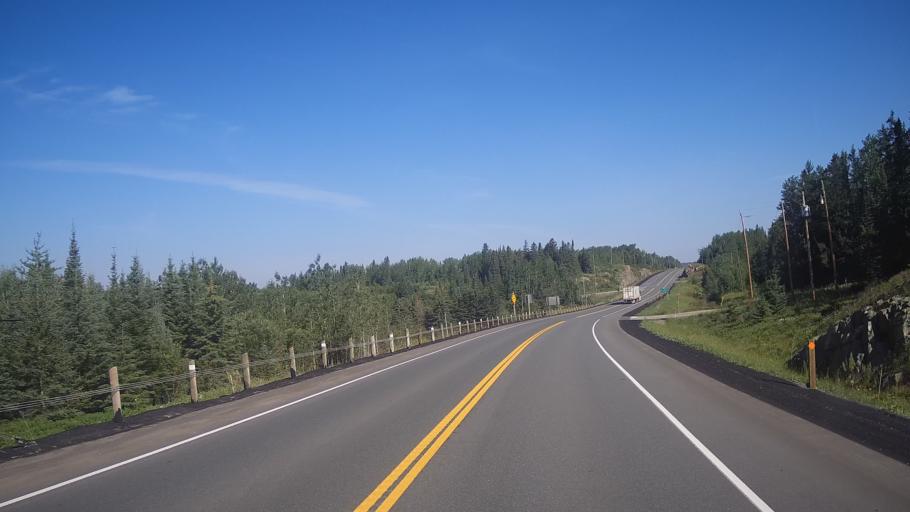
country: CA
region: Ontario
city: Dryden
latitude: 49.6521
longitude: -92.4745
